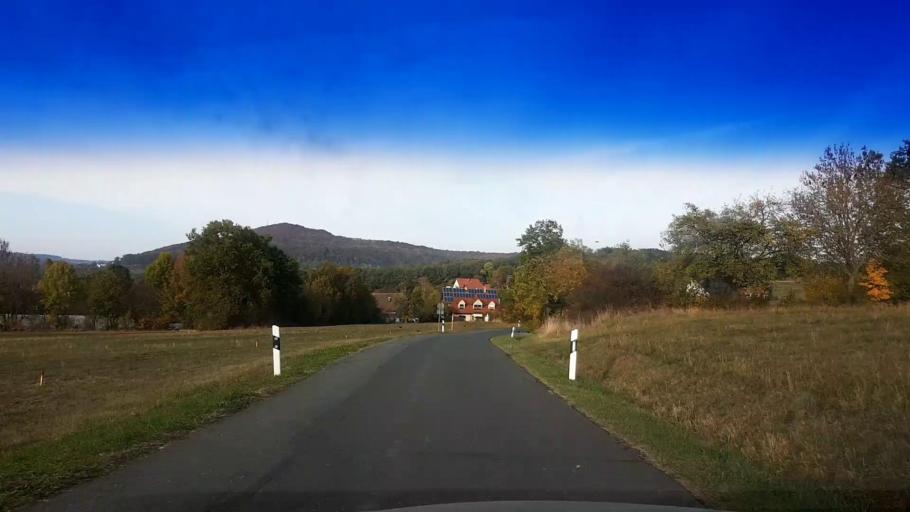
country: DE
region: Bavaria
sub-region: Upper Franconia
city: Schesslitz
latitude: 49.9677
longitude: 11.0601
